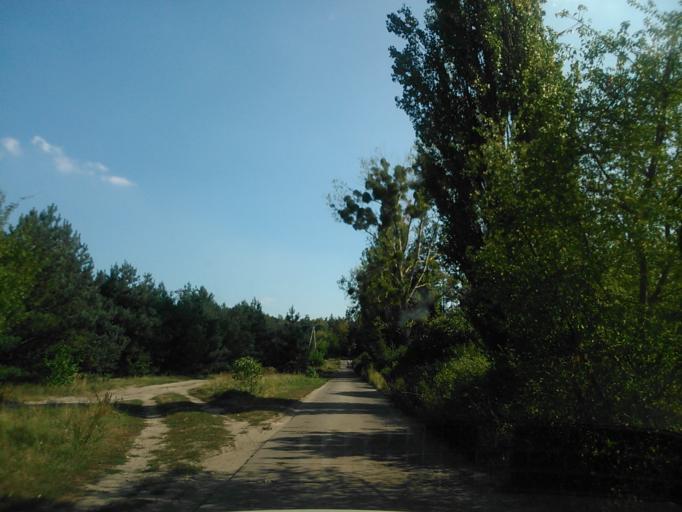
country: PL
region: Kujawsko-Pomorskie
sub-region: Powiat golubsko-dobrzynski
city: Golub-Dobrzyn
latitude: 53.1109
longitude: 19.0731
